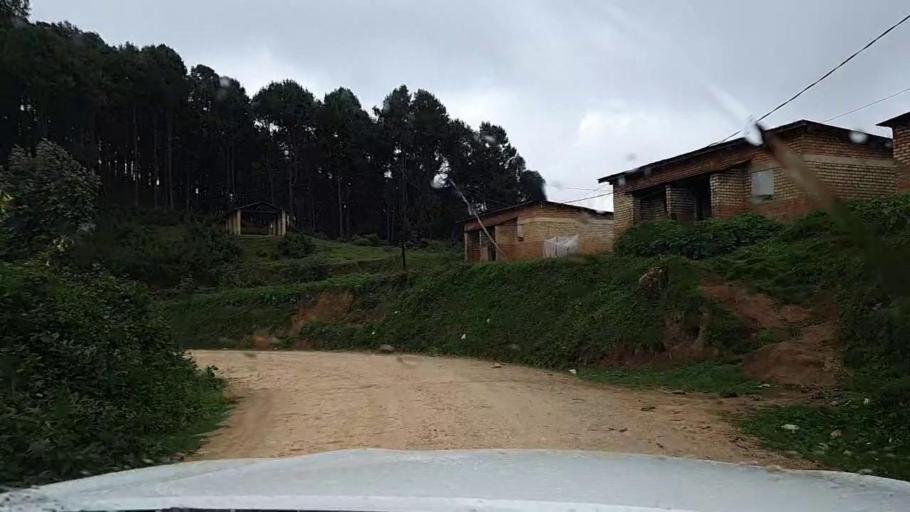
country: RW
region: Southern Province
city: Nzega
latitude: -2.3696
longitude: 29.3830
